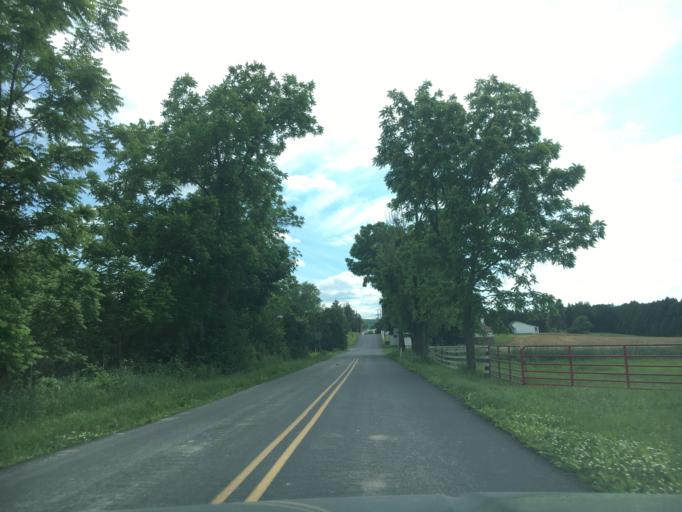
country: US
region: Pennsylvania
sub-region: Berks County
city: Fleetwood
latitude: 40.4618
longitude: -75.8154
